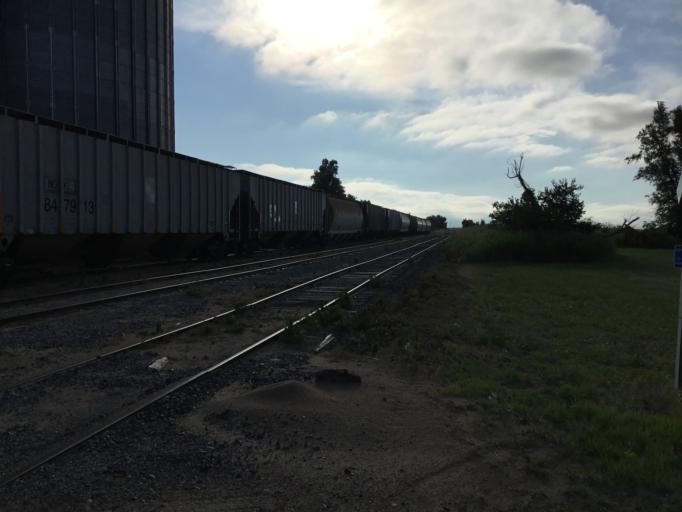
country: US
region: Kansas
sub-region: Barber County
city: Medicine Lodge
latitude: 37.4413
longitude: -98.4199
